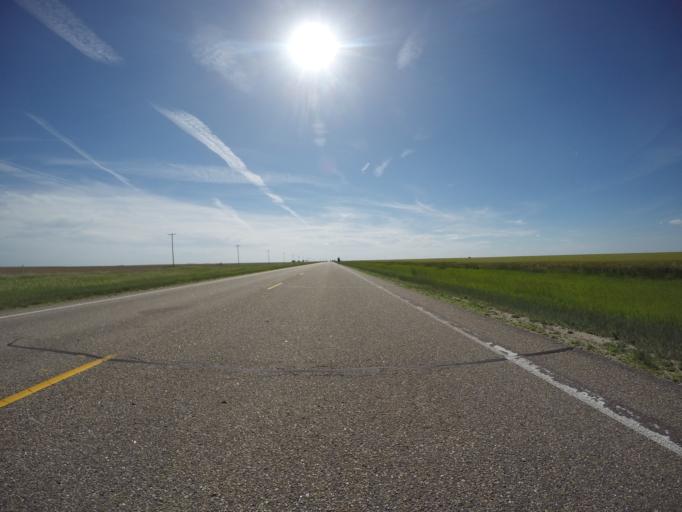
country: US
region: Kansas
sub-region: Cheyenne County
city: Saint Francis
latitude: 39.7567
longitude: -101.9668
